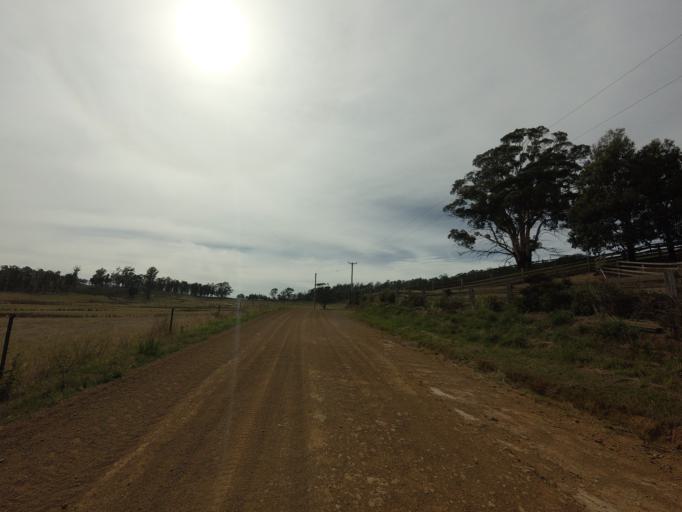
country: AU
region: Tasmania
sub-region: Sorell
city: Sorell
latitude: -42.4812
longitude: 147.5786
